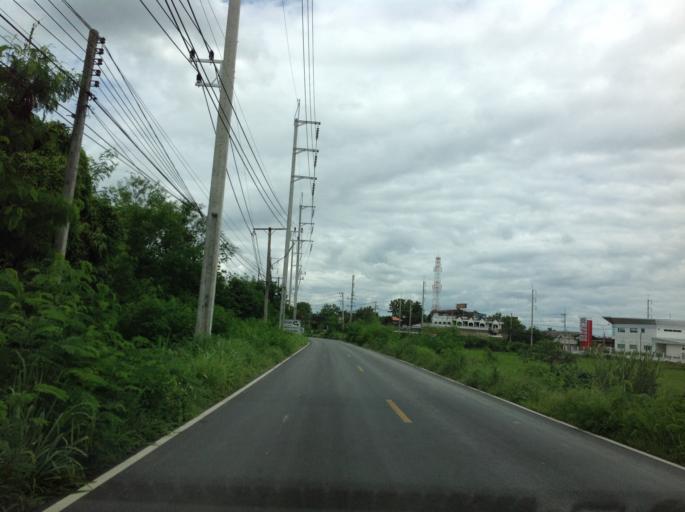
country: TH
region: Chiang Mai
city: Hang Dong
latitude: 18.6735
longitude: 98.9132
